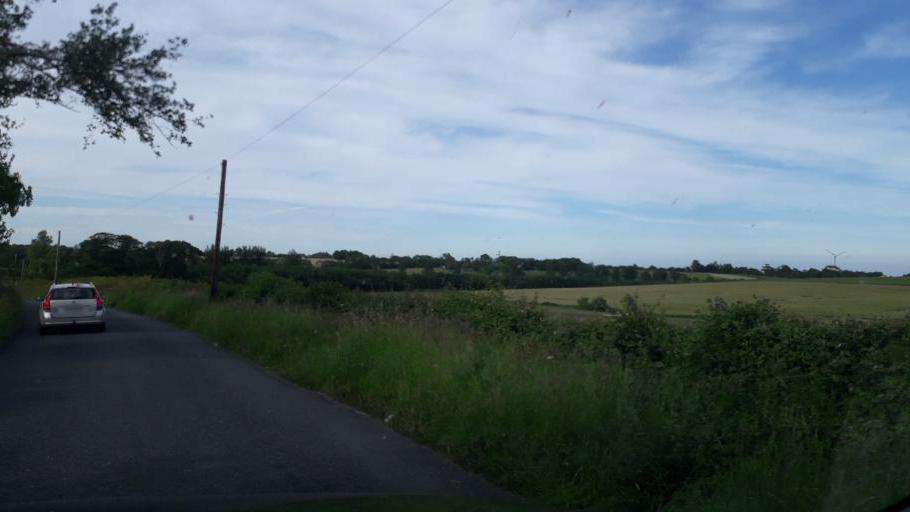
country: IE
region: Leinster
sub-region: Loch Garman
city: Courtown
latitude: 52.5400
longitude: -6.2536
